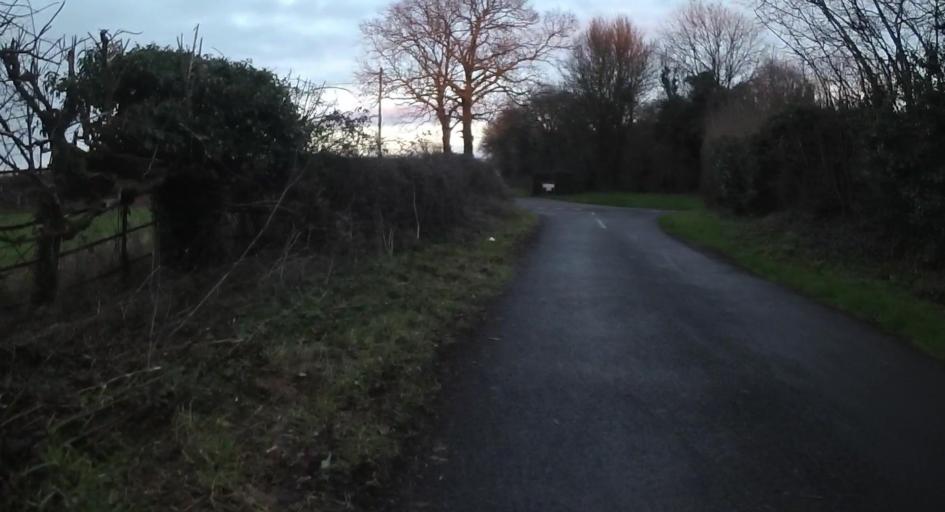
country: GB
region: England
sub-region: Hampshire
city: Four Marks
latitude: 51.0437
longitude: -1.0855
